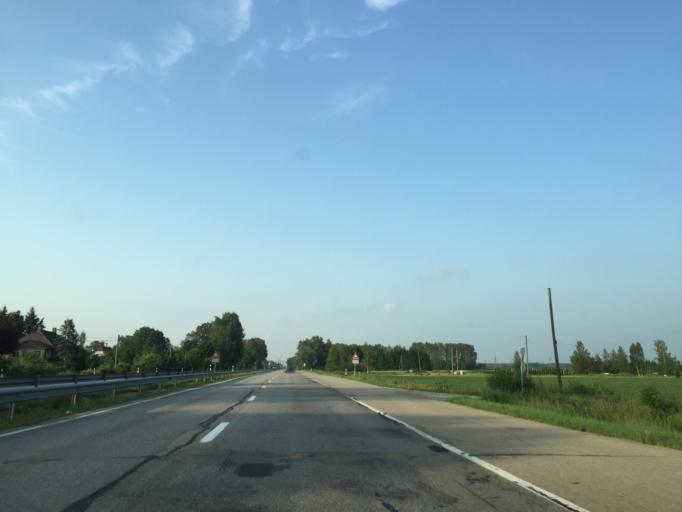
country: LV
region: Olaine
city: Olaine
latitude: 56.7799
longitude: 23.9420
